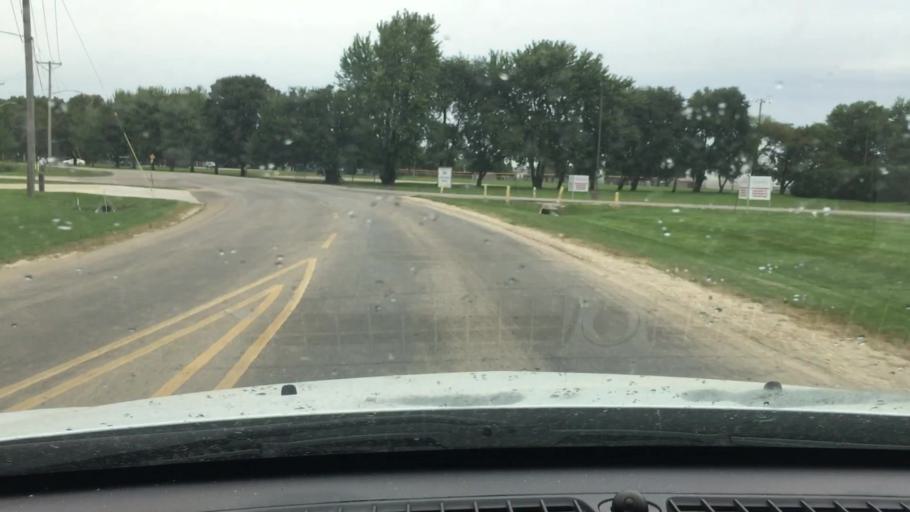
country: US
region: Illinois
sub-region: Ogle County
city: Rochelle
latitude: 41.9088
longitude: -89.0551
